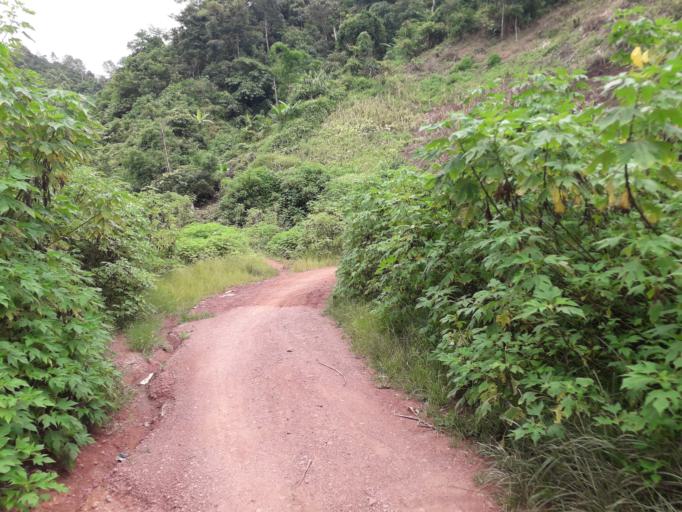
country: CN
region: Yunnan
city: Menglie
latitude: 22.2463
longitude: 101.6096
